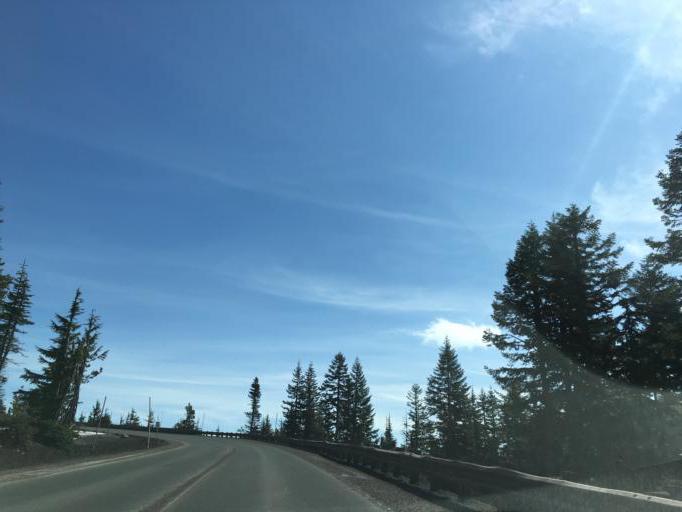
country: US
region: Oregon
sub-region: Clackamas County
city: Mount Hood Village
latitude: 45.3060
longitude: -121.7034
